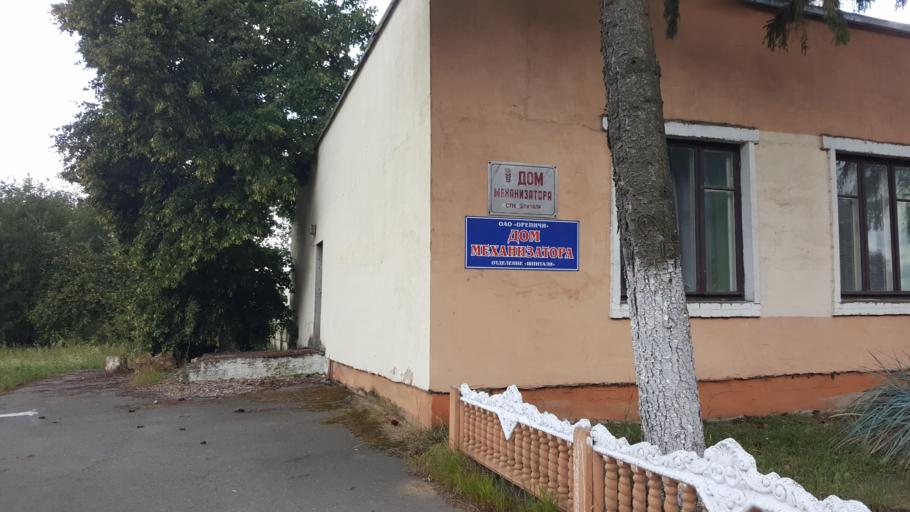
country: BY
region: Brest
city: Zhabinka
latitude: 52.2579
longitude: 23.9805
